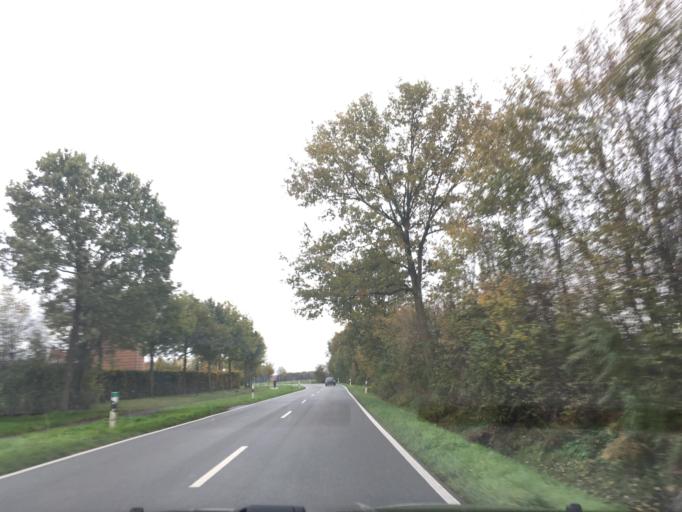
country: DE
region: North Rhine-Westphalia
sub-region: Regierungsbezirk Munster
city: Vreden
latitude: 52.0539
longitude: 6.7722
